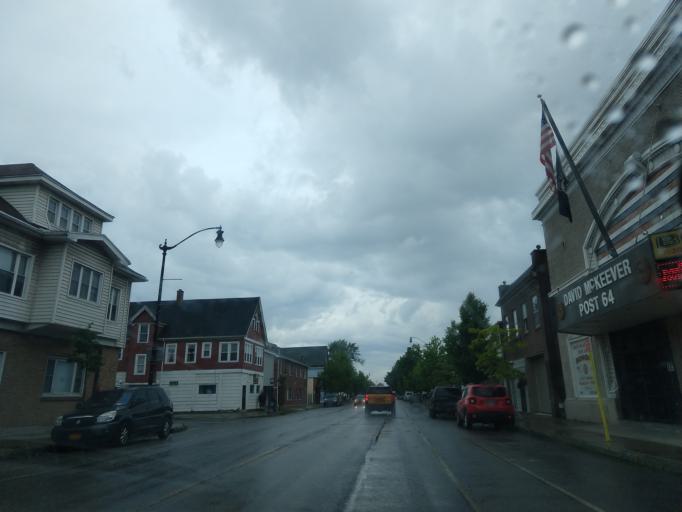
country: US
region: New York
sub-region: Erie County
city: West Seneca
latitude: 42.8505
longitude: -78.8243
